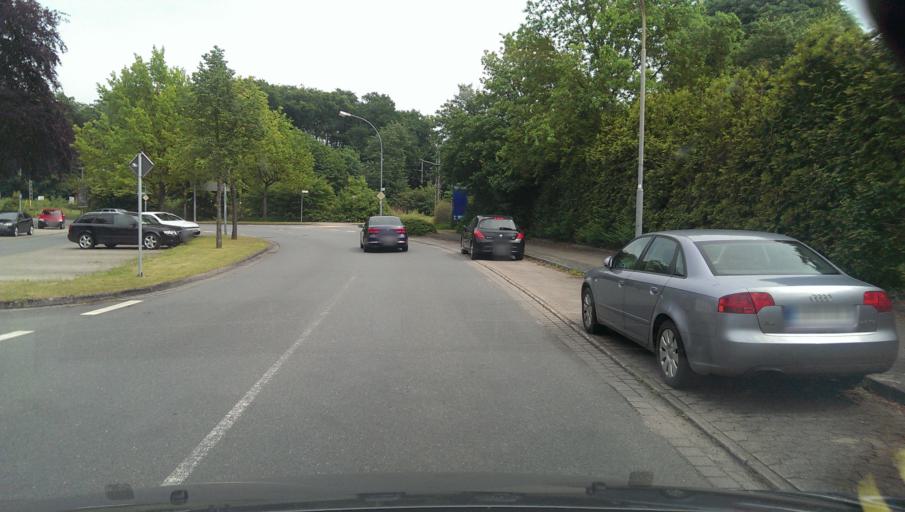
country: DE
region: Lower Saxony
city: Unterluss
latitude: 52.8337
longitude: 10.2977
